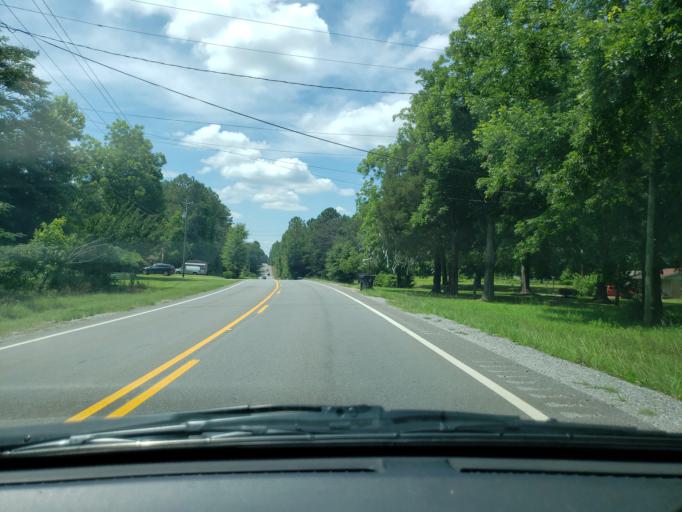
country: US
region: Alabama
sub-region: Elmore County
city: Eclectic
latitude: 32.6227
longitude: -85.9478
